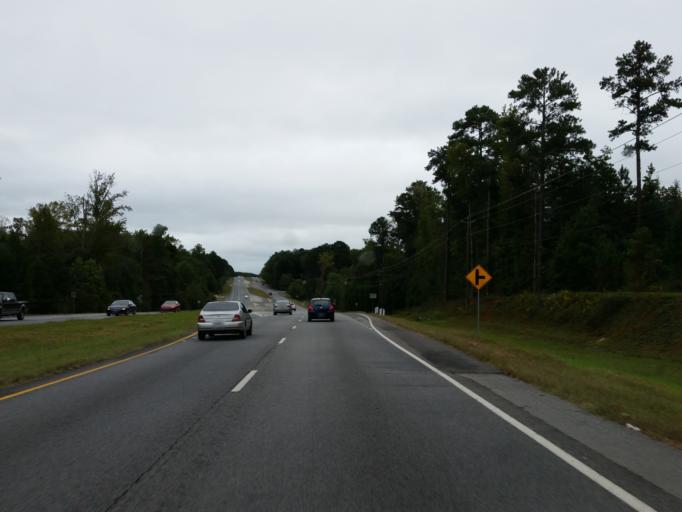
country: US
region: Georgia
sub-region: Clayton County
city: Lovejoy
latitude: 33.4249
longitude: -84.3194
